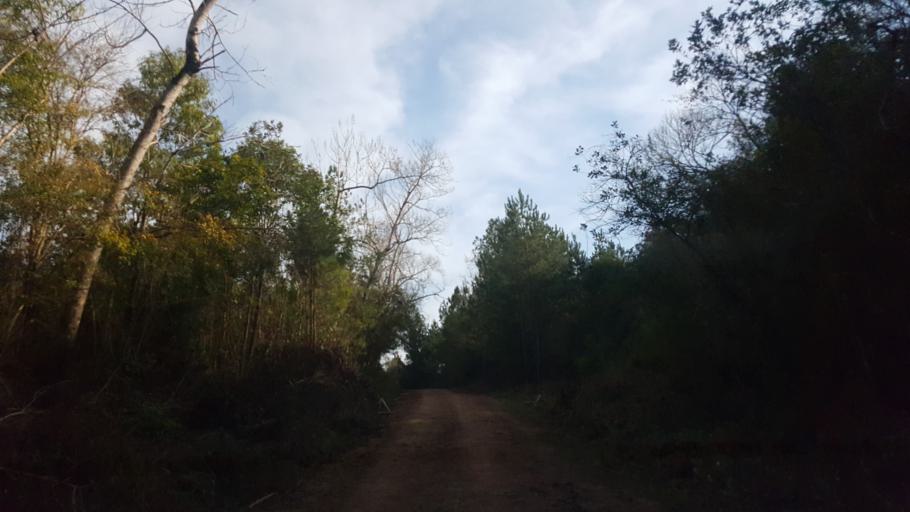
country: AR
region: Misiones
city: Capiovi
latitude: -26.9001
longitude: -55.0915
